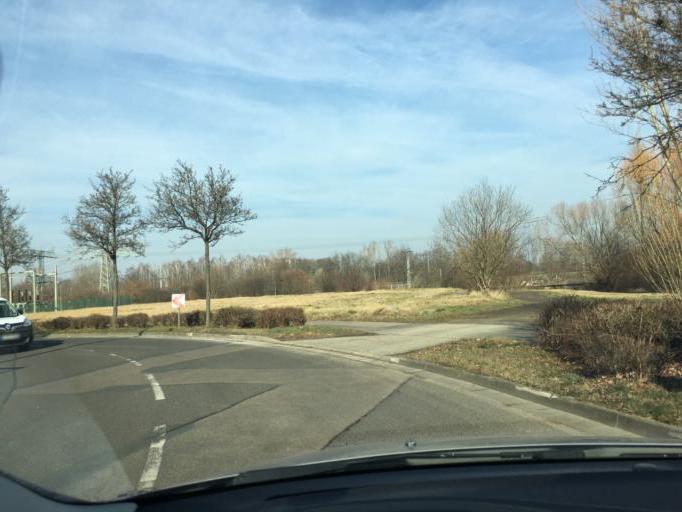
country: DE
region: Saxony
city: Taucha
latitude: 51.3686
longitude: 12.4382
